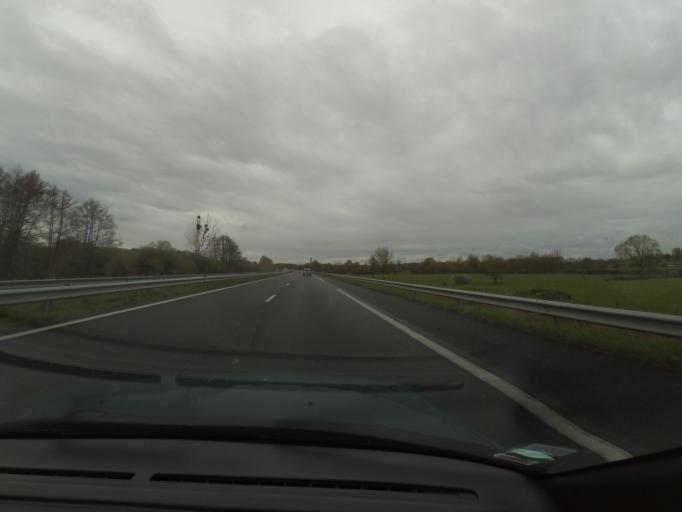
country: FR
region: Pays de la Loire
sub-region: Departement de Maine-et-Loire
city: Durtal
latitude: 47.6916
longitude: -0.2498
